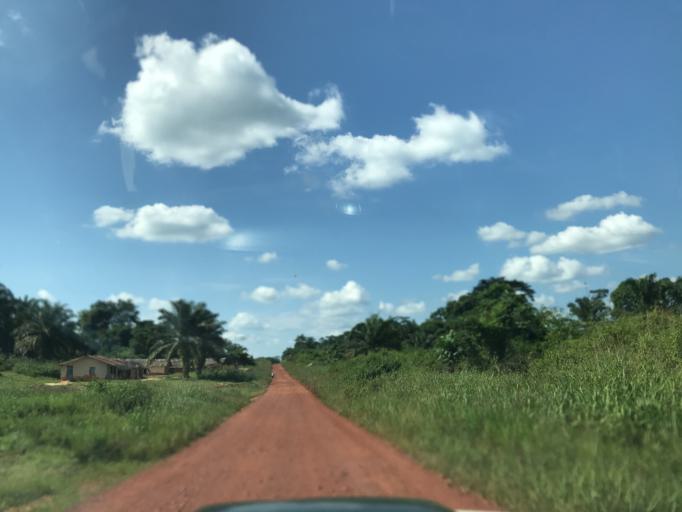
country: CD
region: Eastern Province
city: Kisangani
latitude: 1.2173
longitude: 25.2676
